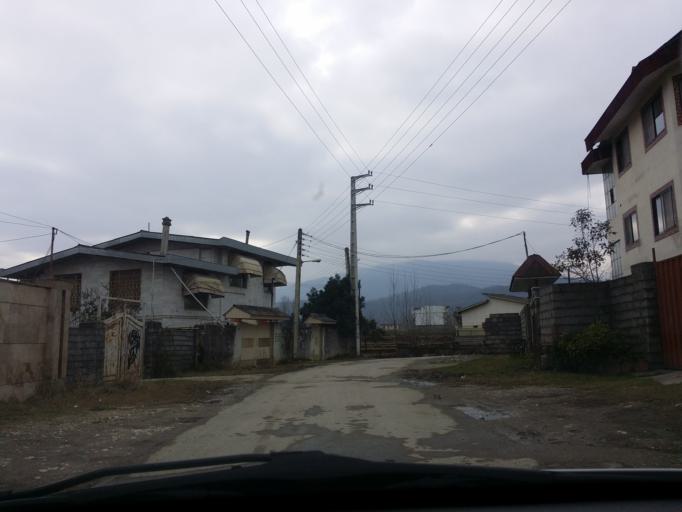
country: IR
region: Mazandaran
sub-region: Nowshahr
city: Nowshahr
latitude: 36.6452
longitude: 51.4745
